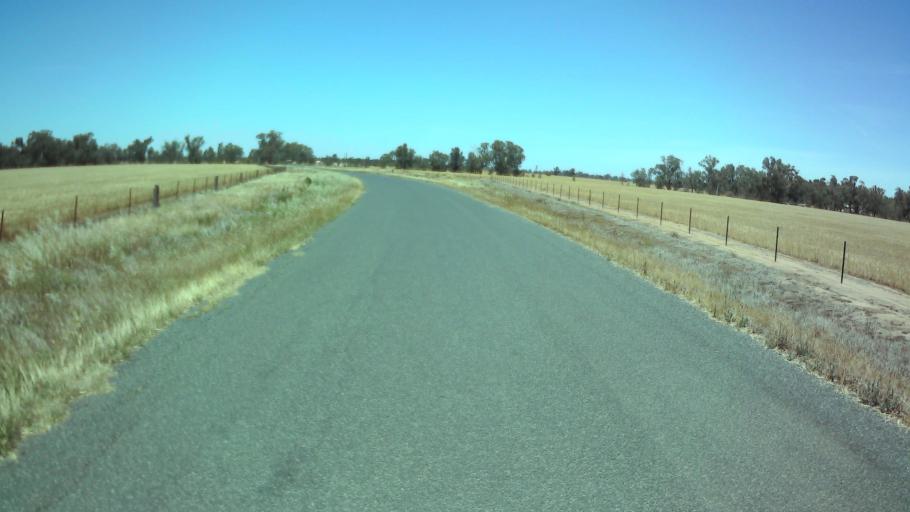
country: AU
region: New South Wales
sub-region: Weddin
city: Grenfell
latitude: -34.0352
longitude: 147.7896
